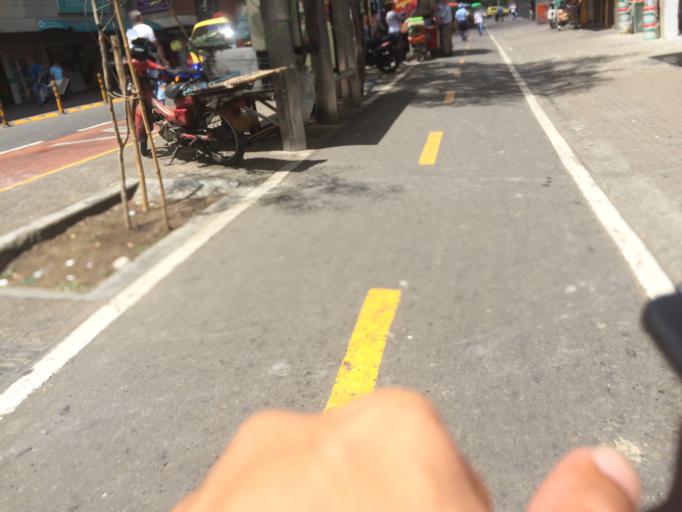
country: CO
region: Antioquia
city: Medellin
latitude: 6.2538
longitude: -75.5684
